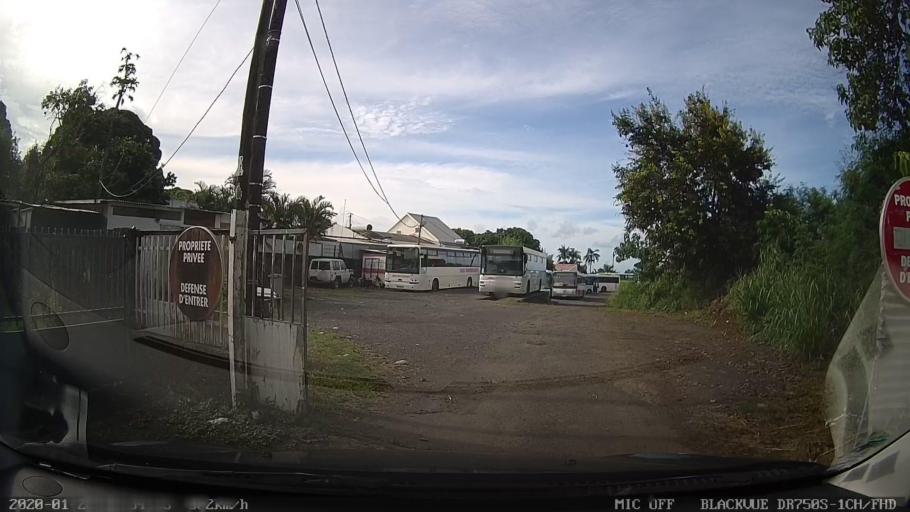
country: RE
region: Reunion
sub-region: Reunion
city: Sainte-Marie
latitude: -20.9090
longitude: 55.5054
